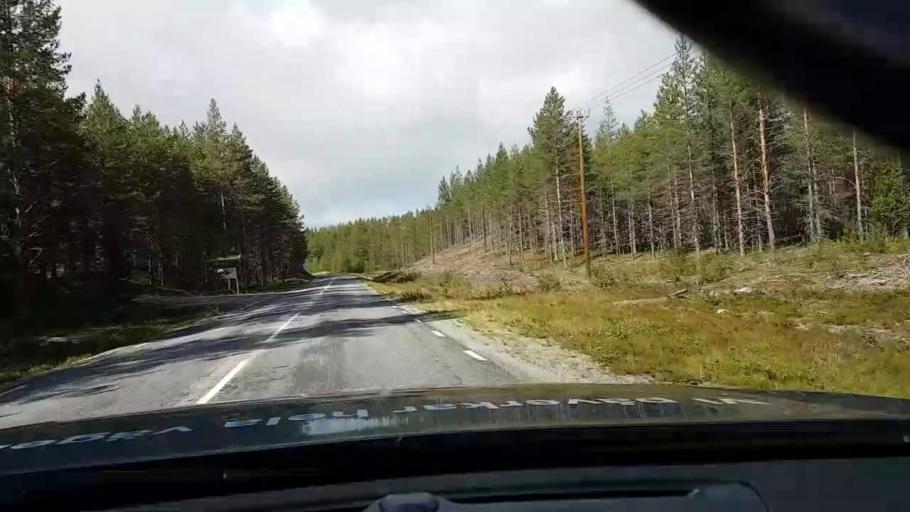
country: SE
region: Vaesterbotten
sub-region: Asele Kommun
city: Asele
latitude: 63.8519
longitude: 17.3939
